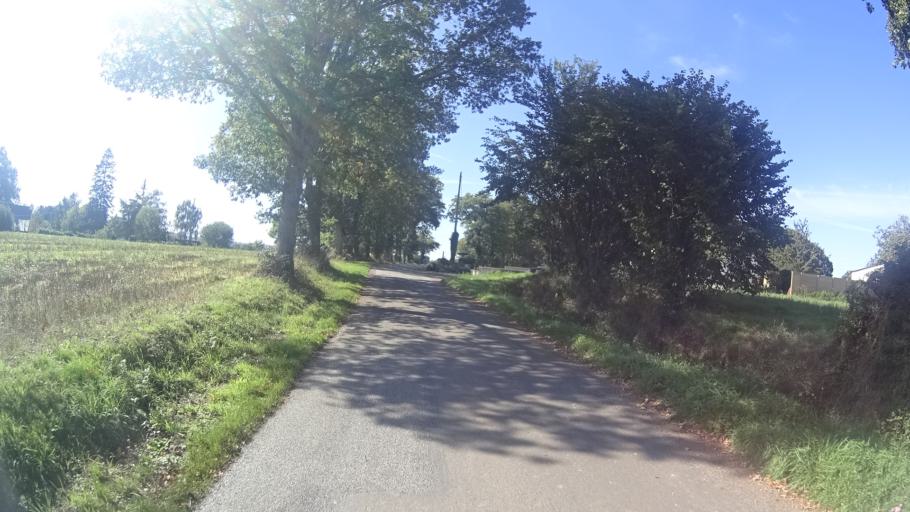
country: FR
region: Brittany
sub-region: Departement du Morbihan
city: Peillac
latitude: 47.7406
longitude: -2.2017
